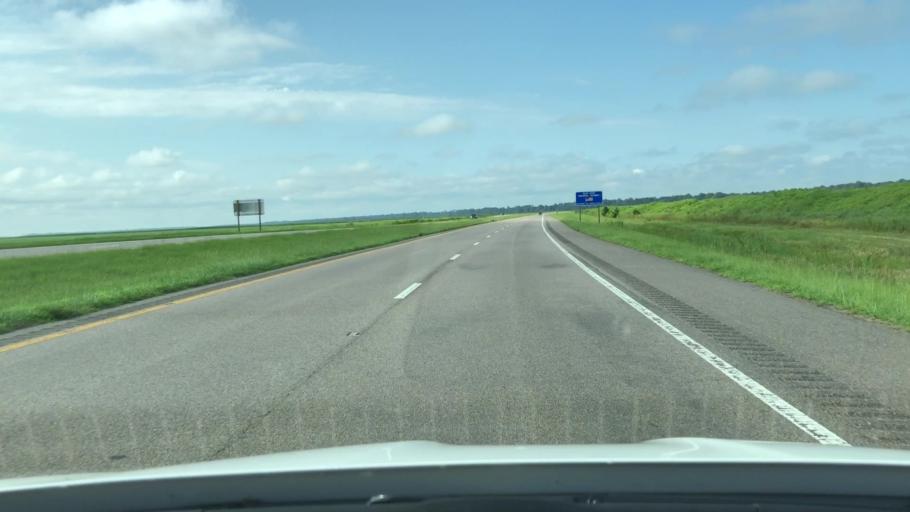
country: US
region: North Carolina
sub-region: Currituck County
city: Moyock
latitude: 36.5932
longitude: -76.3788
